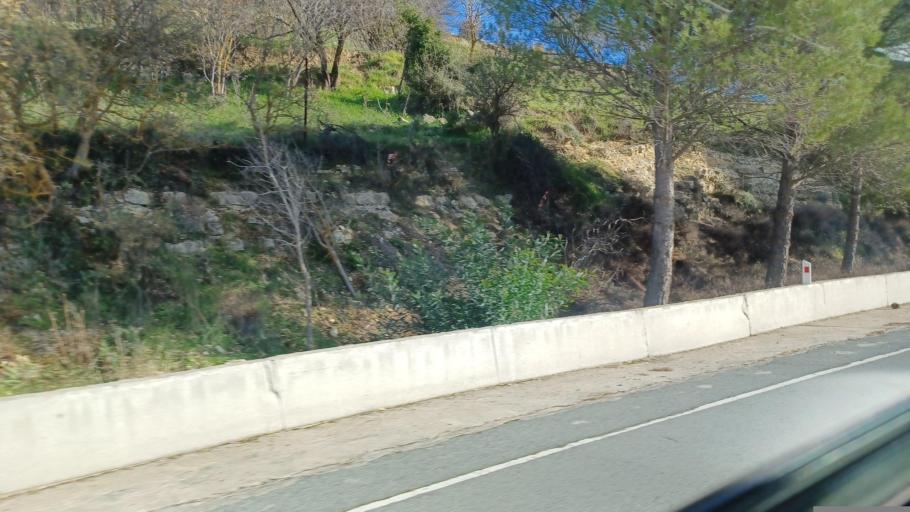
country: CY
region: Limassol
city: Pachna
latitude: 34.8304
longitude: 32.7954
